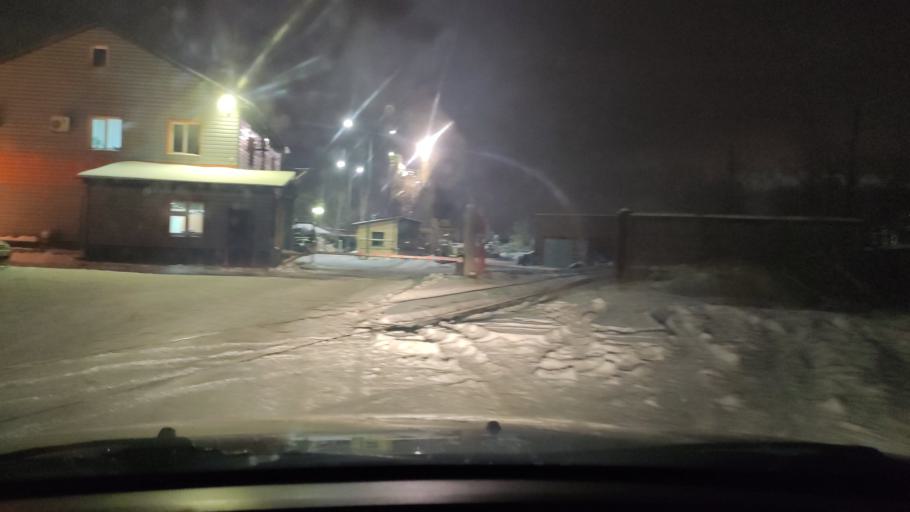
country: RU
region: Perm
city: Kondratovo
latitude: 57.9318
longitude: 56.1455
